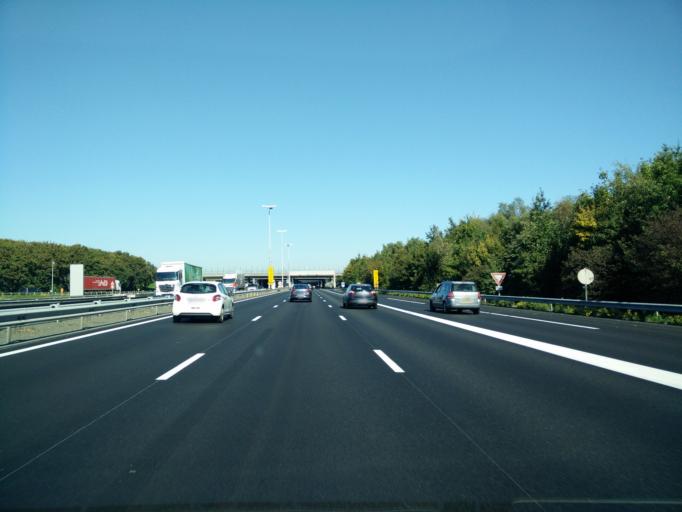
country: FR
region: Ile-de-France
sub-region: Departement du Val-d'Oise
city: Roissy-en-France
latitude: 49.0139
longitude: 2.5306
